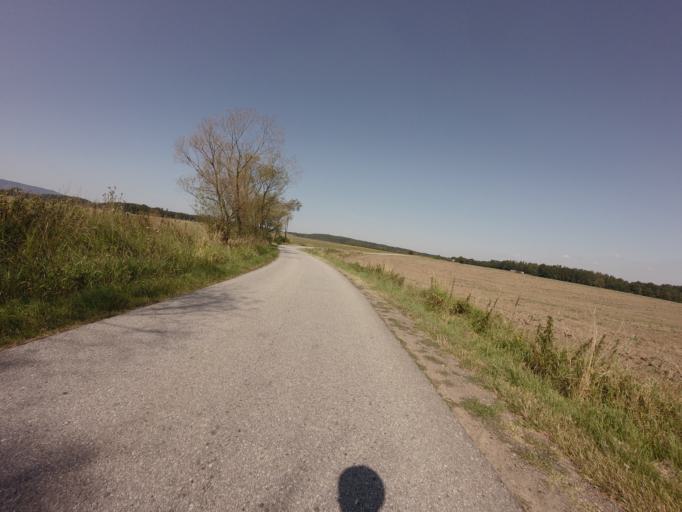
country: CZ
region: Jihocesky
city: Kamenny Ujezd
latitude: 48.9067
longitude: 14.4362
